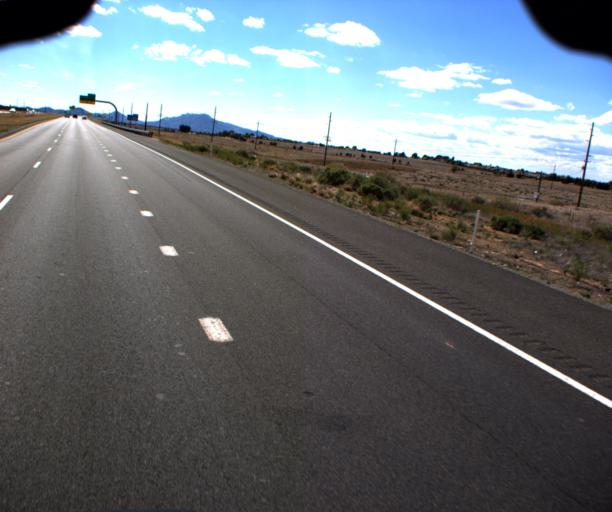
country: US
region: Arizona
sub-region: Yavapai County
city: Prescott Valley
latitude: 34.6396
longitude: -112.3213
